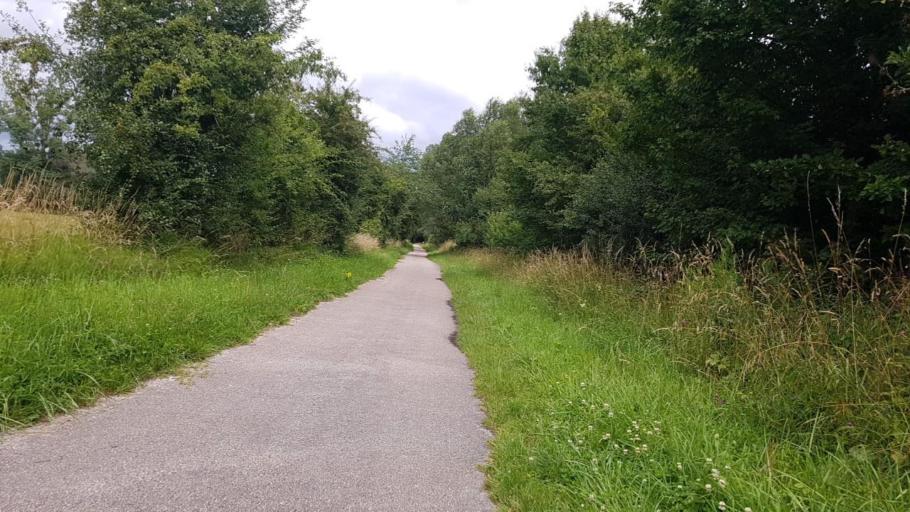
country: FR
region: Picardie
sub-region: Departement de l'Aisne
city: Esqueheries
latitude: 49.8998
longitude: 3.7515
